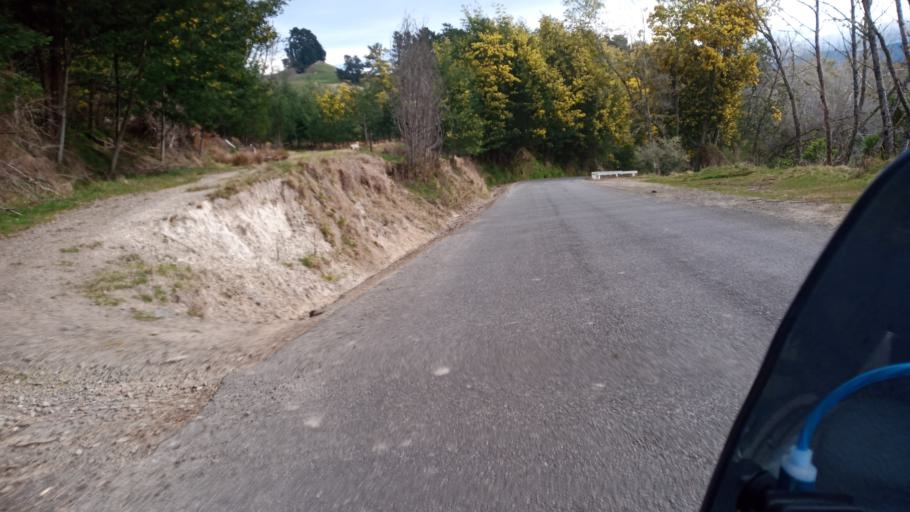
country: NZ
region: Hawke's Bay
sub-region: Wairoa District
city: Wairoa
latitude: -38.7737
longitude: 177.4186
